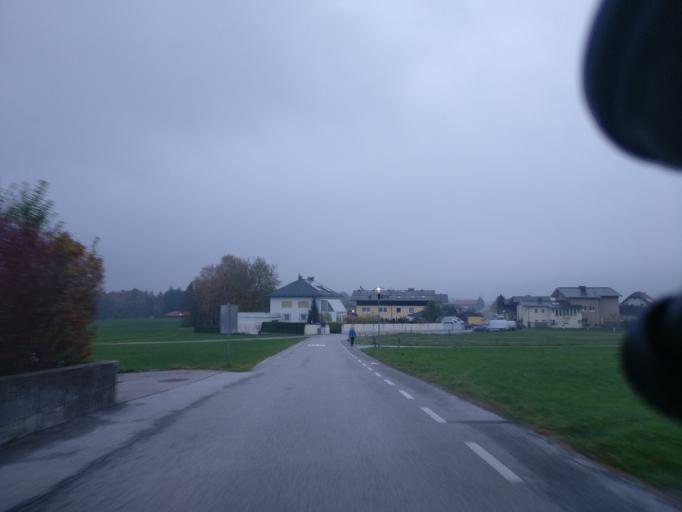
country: AT
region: Salzburg
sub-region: Politischer Bezirk Salzburg-Umgebung
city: Elixhausen
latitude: 47.8672
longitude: 13.0714
